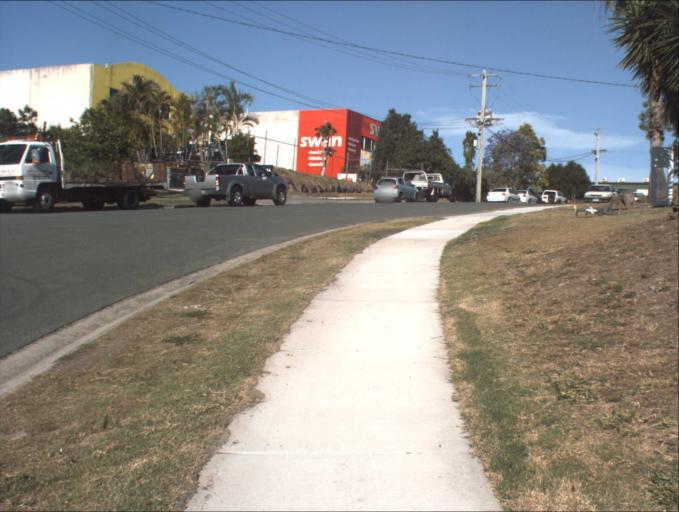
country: AU
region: Queensland
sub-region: Logan
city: Beenleigh
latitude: -27.7143
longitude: 153.1823
